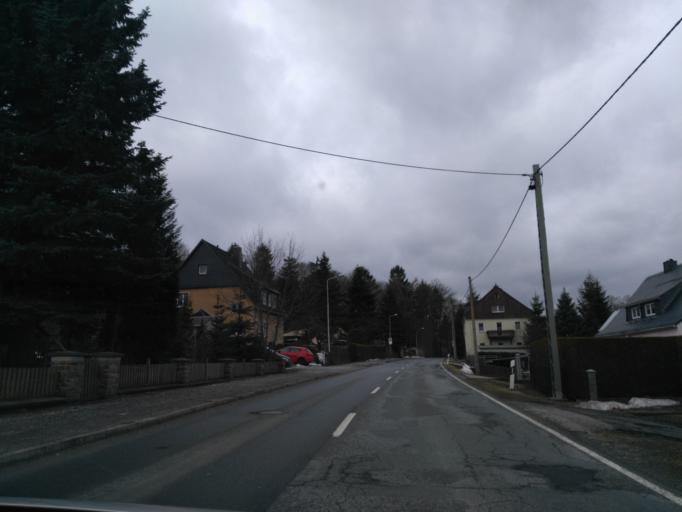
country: DE
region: Saxony
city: Annaberg-Buchholz
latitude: 50.5856
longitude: 13.0225
